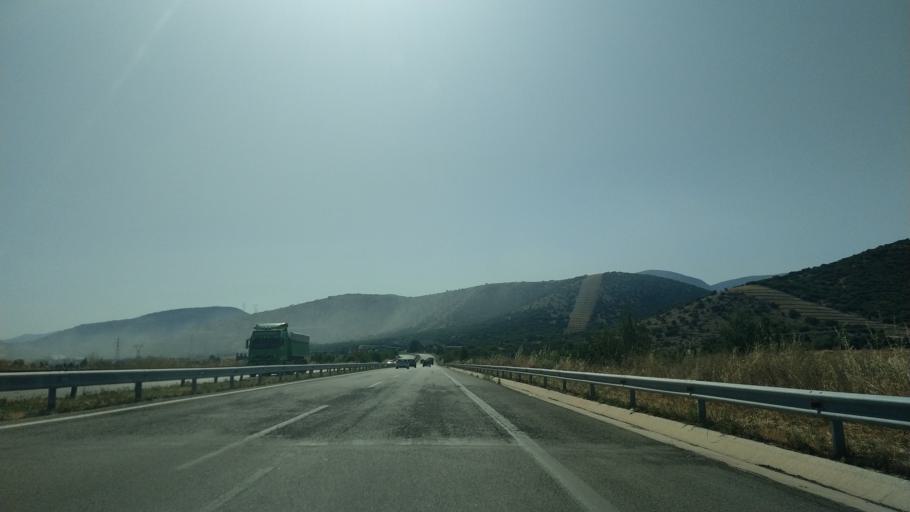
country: GR
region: East Macedonia and Thrace
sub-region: Nomos Kavalas
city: Nea Karvali
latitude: 40.9703
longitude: 24.5011
